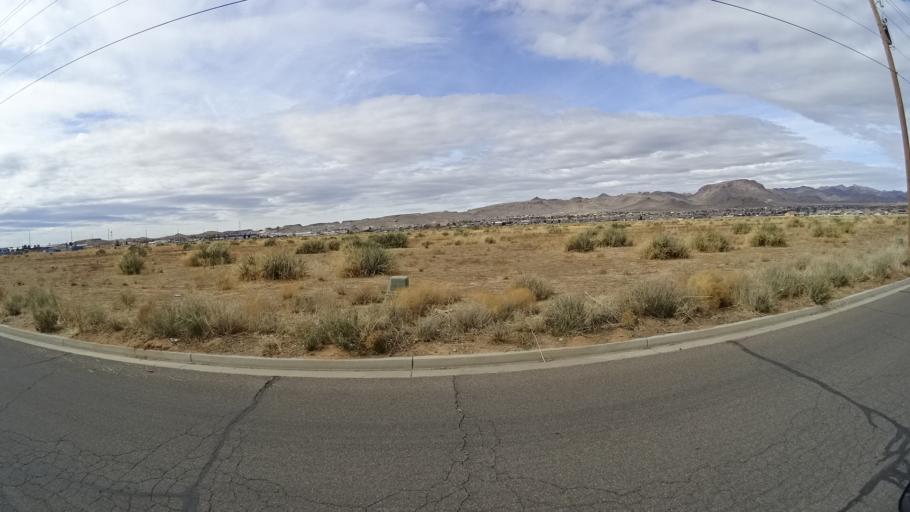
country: US
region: Arizona
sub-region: Mohave County
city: New Kingman-Butler
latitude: 35.2278
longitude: -114.0056
